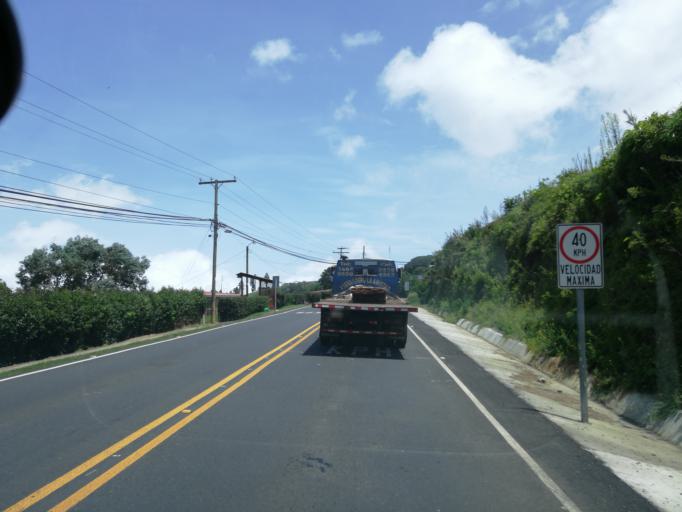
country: CR
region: Alajuela
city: Zarcero
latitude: 10.2158
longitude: -84.3994
